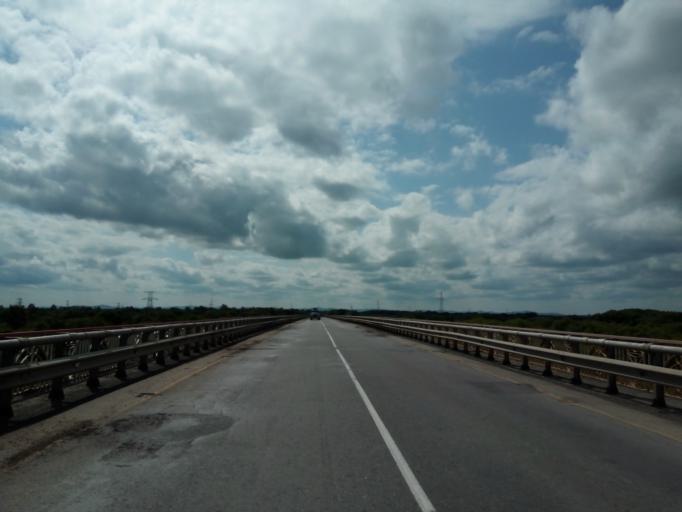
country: RU
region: Primorskiy
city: Dal'nerechensk
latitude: 45.9606
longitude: 133.7838
